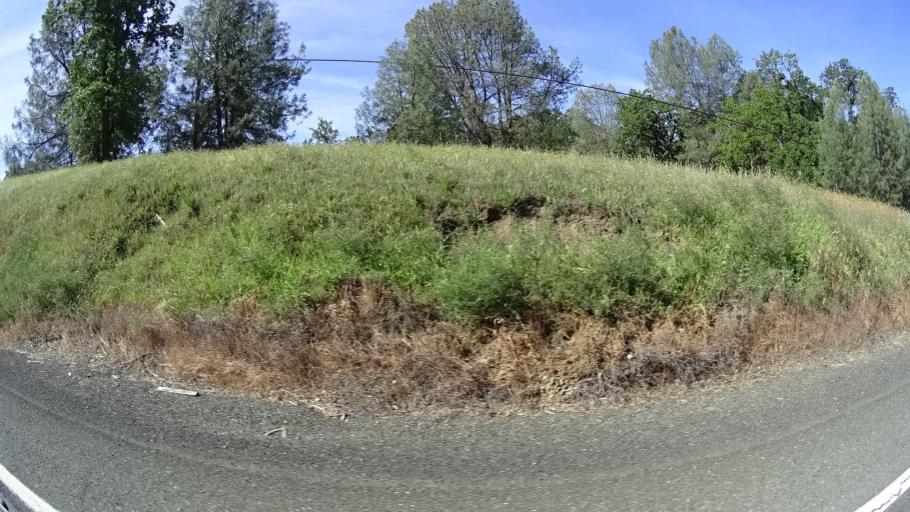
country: US
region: California
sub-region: Lake County
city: Kelseyville
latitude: 38.9478
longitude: -122.8237
